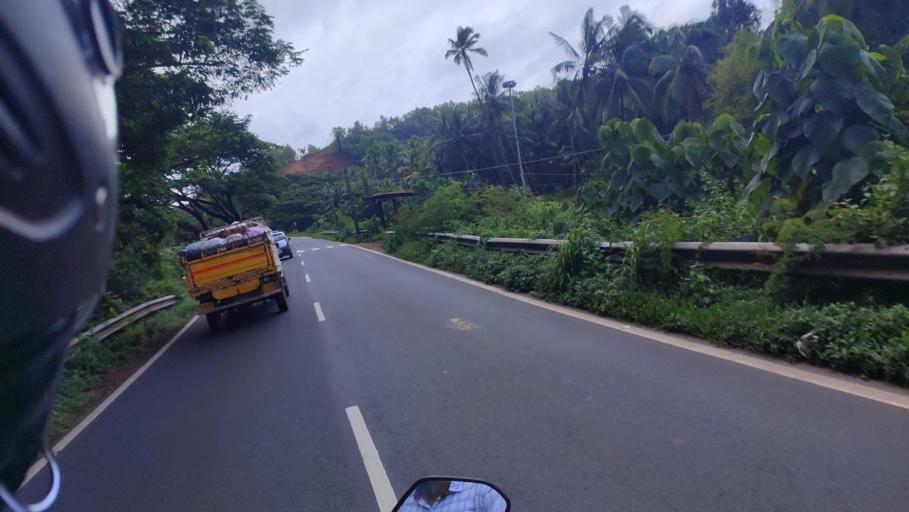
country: IN
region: Kerala
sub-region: Kasaragod District
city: Nileshwar
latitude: 12.2384
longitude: 75.1502
